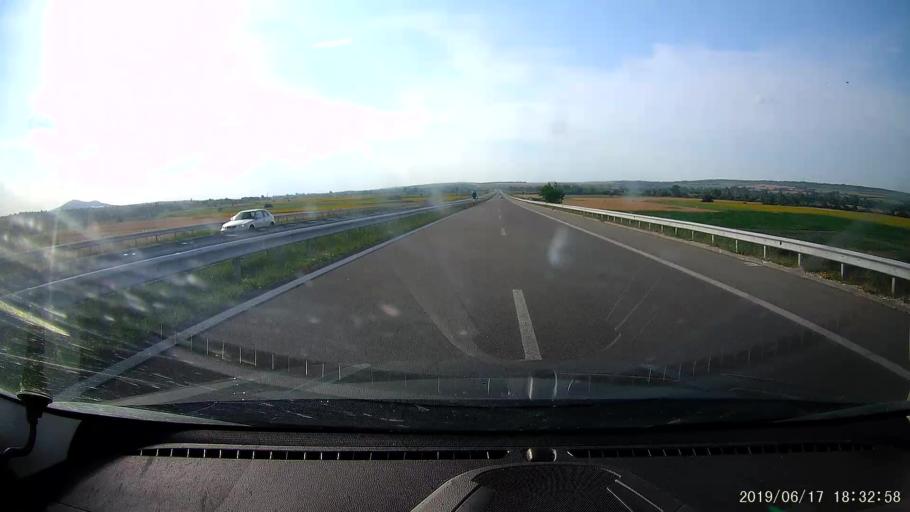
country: BG
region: Khaskovo
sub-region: Obshtina Dimitrovgrad
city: Dimitrovgrad
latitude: 42.0696
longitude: 25.4676
